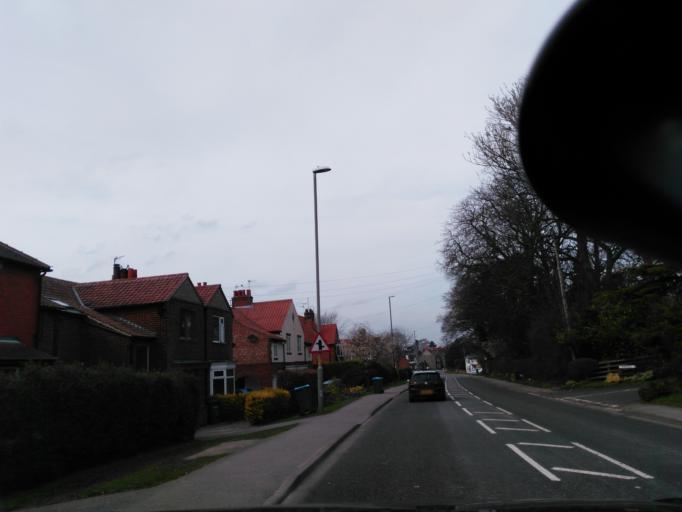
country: GB
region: England
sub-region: North Yorkshire
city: Northallerton
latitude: 54.3314
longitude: -1.4312
